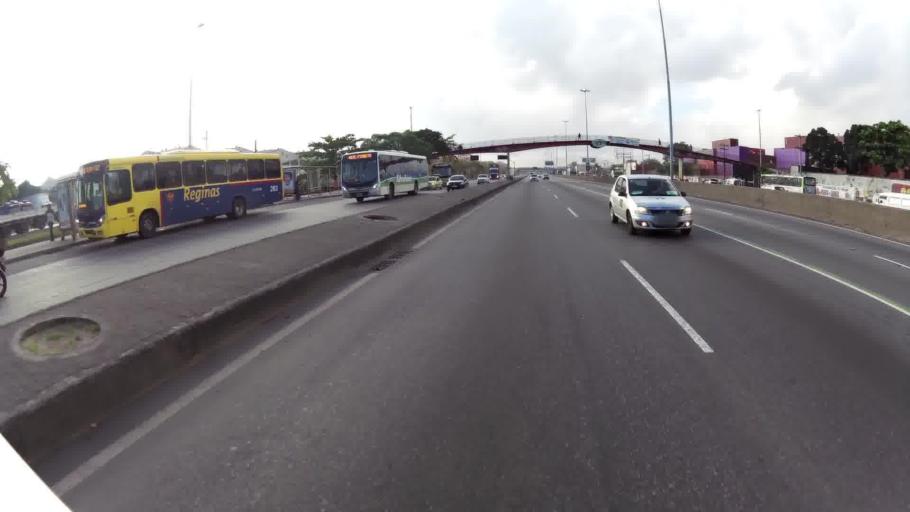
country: BR
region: Rio de Janeiro
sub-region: Duque De Caxias
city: Duque de Caxias
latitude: -22.8218
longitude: -43.2810
